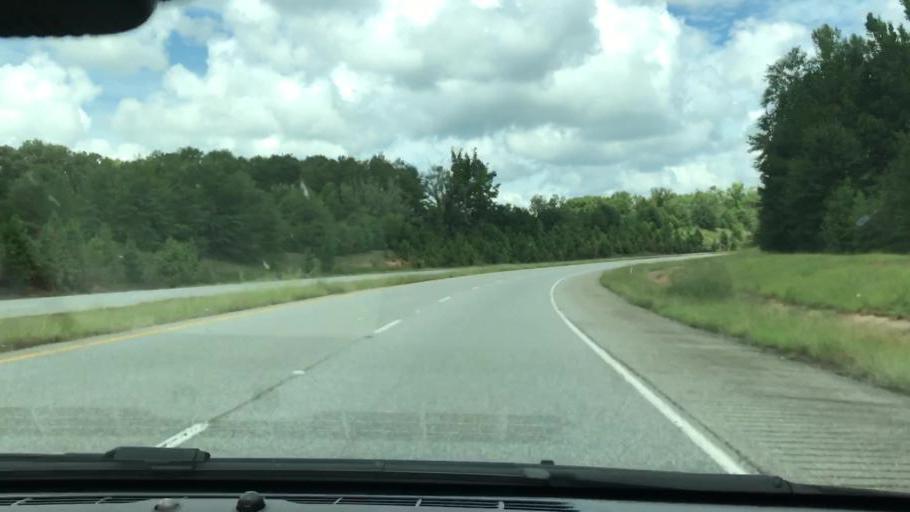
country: US
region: Georgia
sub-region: Stewart County
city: Lumpkin
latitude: 32.1608
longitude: -84.8305
